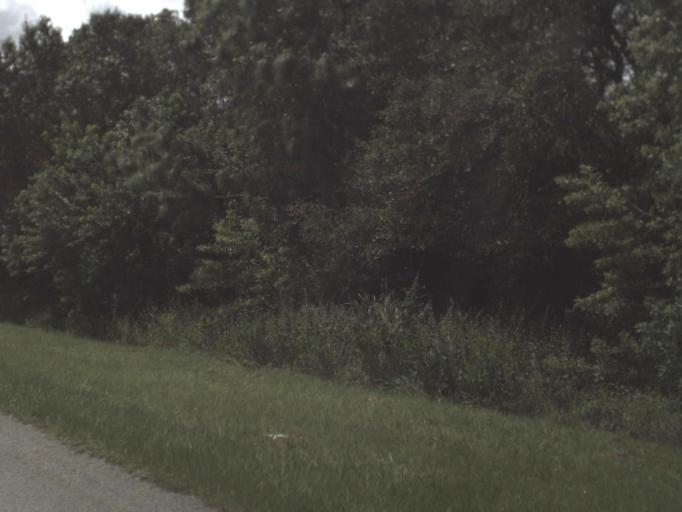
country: US
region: Florida
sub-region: Collier County
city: Immokalee
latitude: 26.3204
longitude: -81.3431
